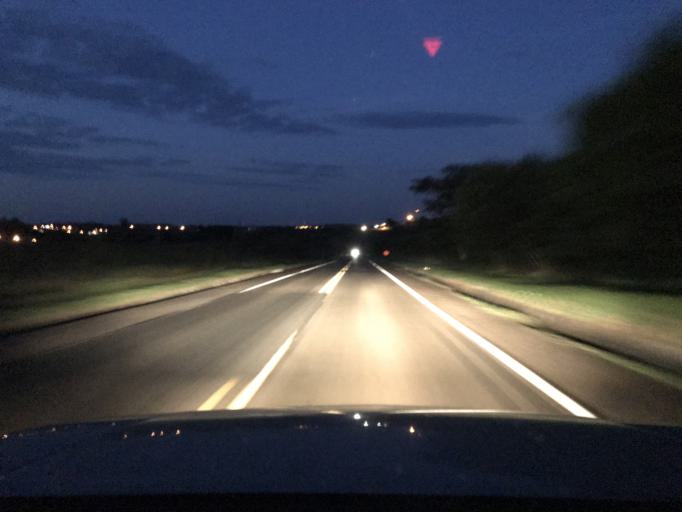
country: PY
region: Canindeyu
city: Salto del Guaira
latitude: -24.1057
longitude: -54.2375
